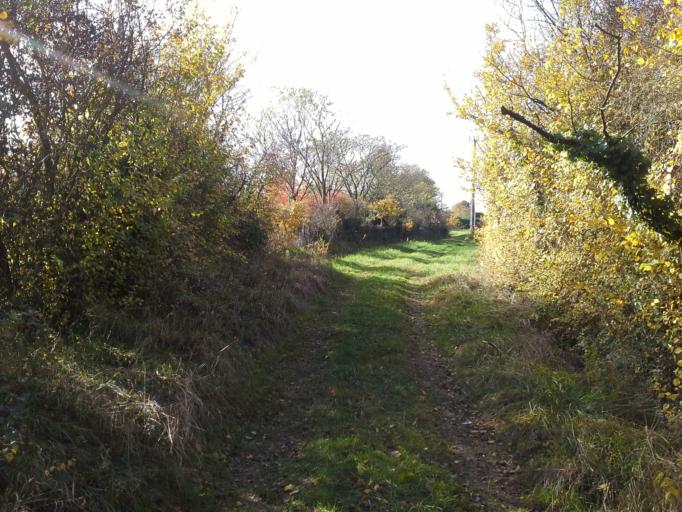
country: FR
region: Poitou-Charentes
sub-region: Departement de la Vienne
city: Pleumartin
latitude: 46.6354
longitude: 0.7569
